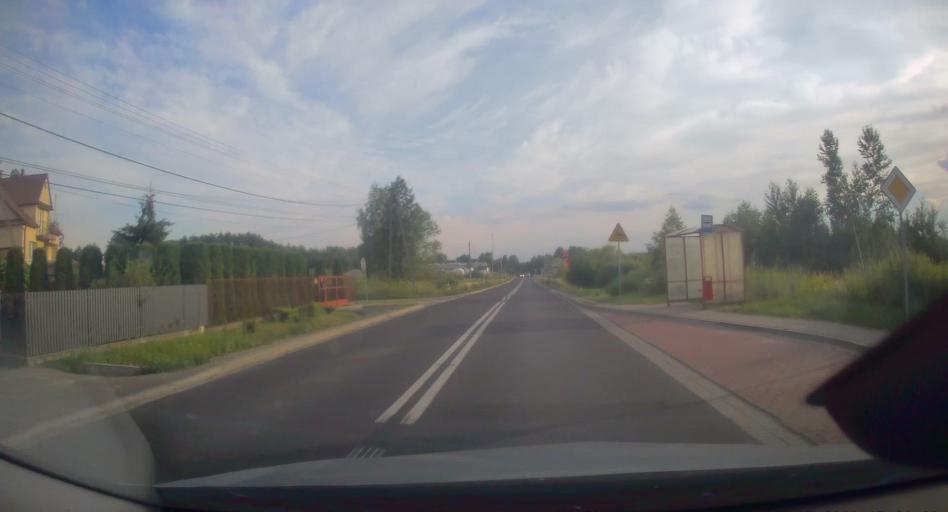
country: PL
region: Lesser Poland Voivodeship
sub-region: Powiat brzeski
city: Przyborow
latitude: 50.0312
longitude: 20.6406
